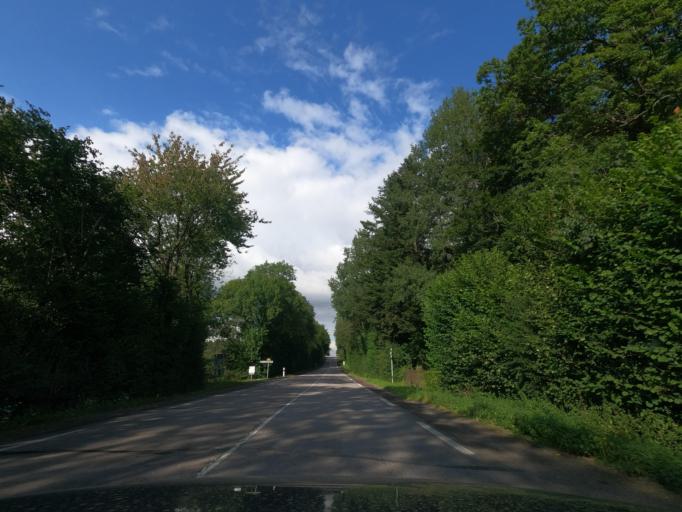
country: FR
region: Lower Normandy
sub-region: Departement de l'Orne
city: Gace
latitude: 48.8294
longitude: 0.3344
